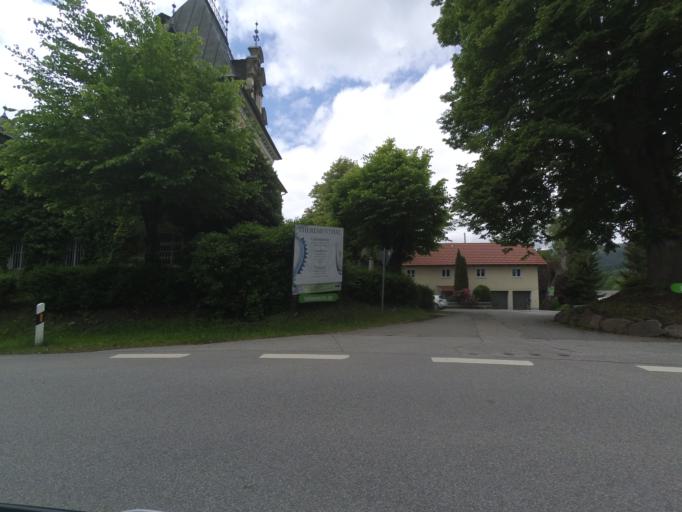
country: DE
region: Bavaria
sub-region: Lower Bavaria
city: Zwiesel
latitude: 49.0304
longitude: 13.2324
